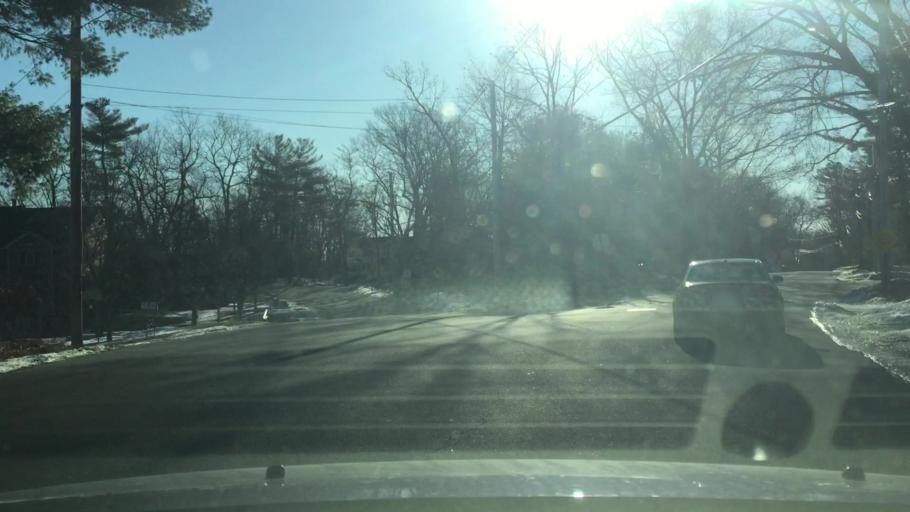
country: US
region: Massachusetts
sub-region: Middlesex County
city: Dracut
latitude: 42.6656
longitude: -71.3438
